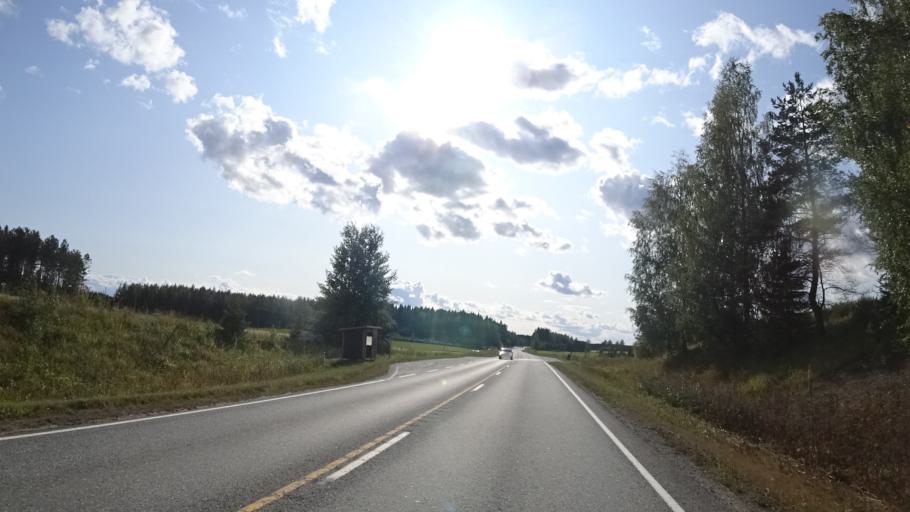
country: FI
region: North Karelia
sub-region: Keski-Karjala
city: Kitee
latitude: 62.0949
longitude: 30.0627
